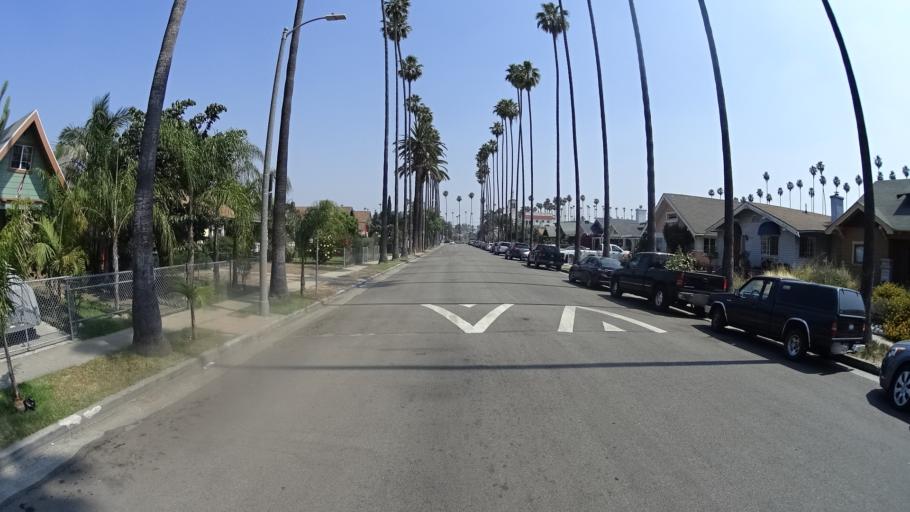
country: US
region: California
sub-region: Los Angeles County
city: View Park-Windsor Hills
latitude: 34.0238
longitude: -118.3201
